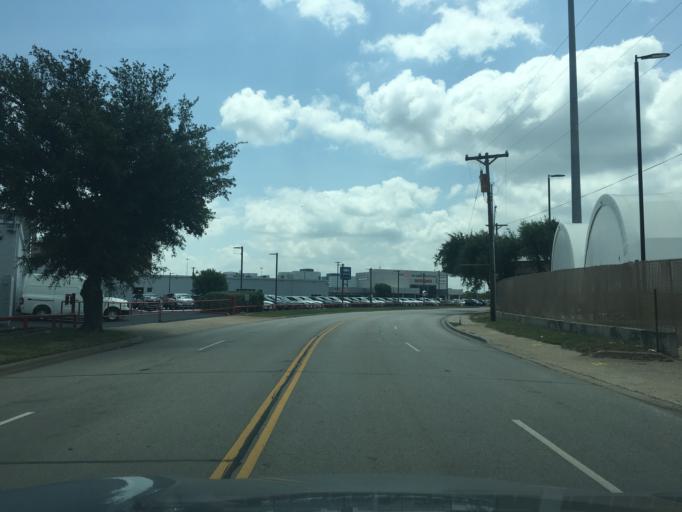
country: US
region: Texas
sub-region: Dallas County
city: Addison
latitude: 32.9280
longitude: -96.8303
